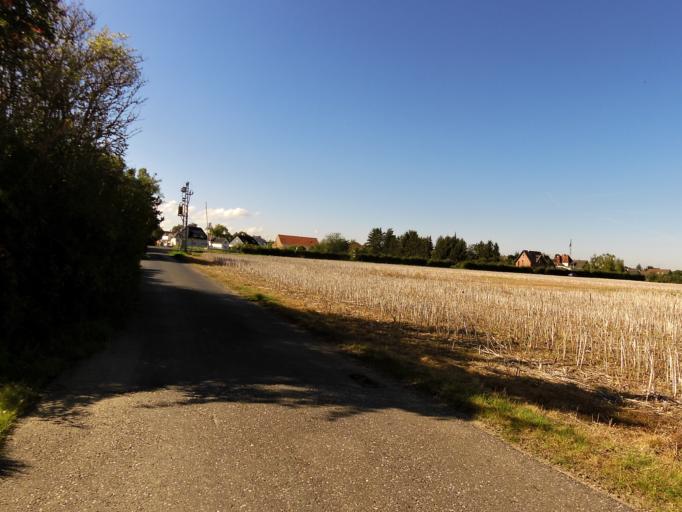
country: DE
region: North Rhine-Westphalia
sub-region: Regierungsbezirk Koln
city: Rheinbach
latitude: 50.6486
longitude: 6.8915
